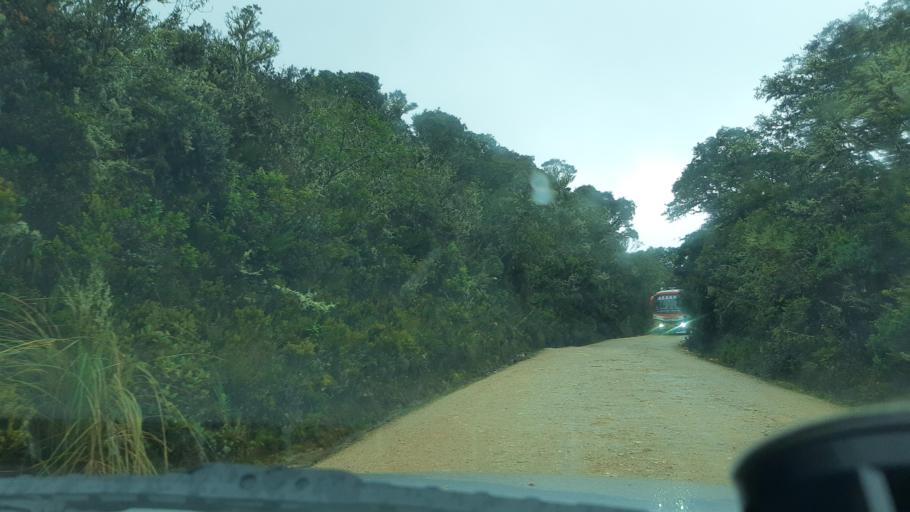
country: CO
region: Cundinamarca
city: Villapinzon
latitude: 5.2082
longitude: -73.5557
